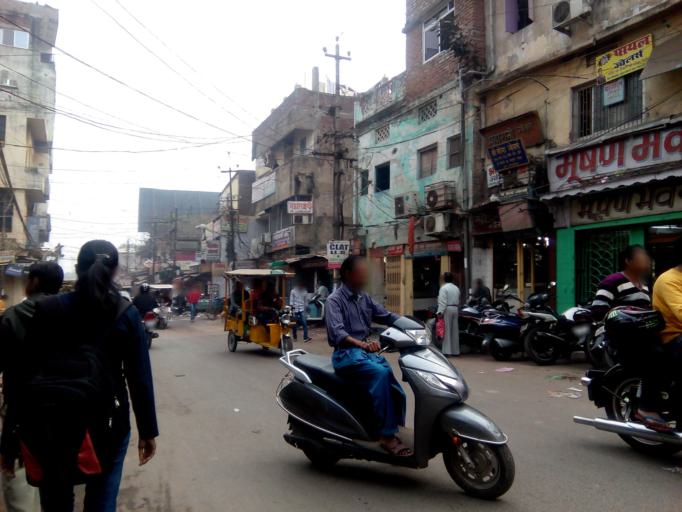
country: IN
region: Bihar
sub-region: Patna
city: Patna
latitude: 25.6152
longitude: 85.1506
